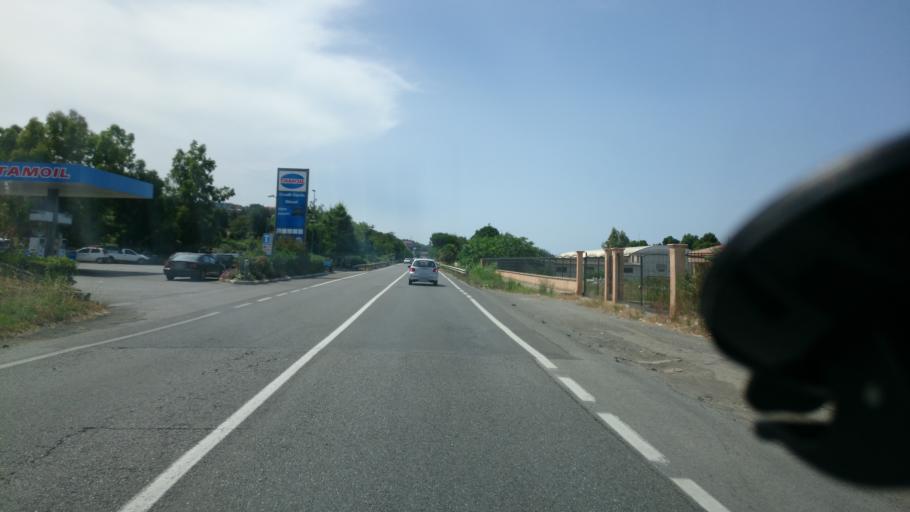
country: IT
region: Calabria
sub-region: Provincia di Cosenza
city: Diamante
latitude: 39.6923
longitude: 15.8168
